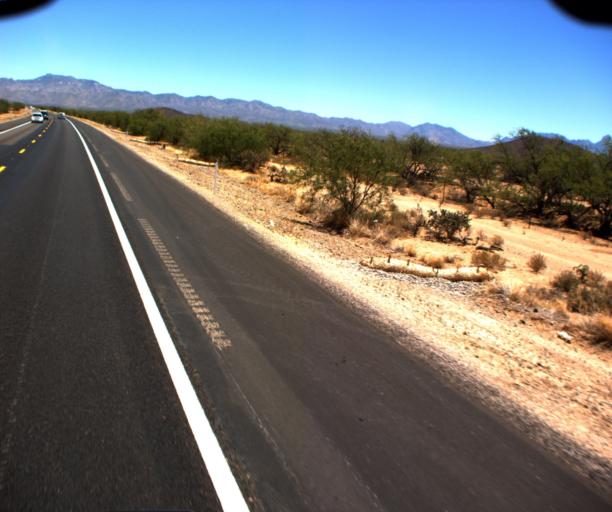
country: US
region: Arizona
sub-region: Pima County
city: Sells
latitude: 31.9197
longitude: -111.8296
